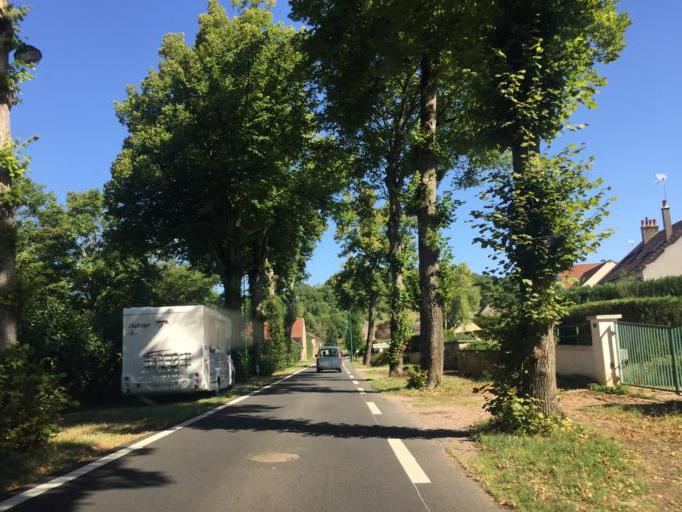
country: FR
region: Bourgogne
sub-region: Departement de la Nievre
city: Clamecy
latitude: 47.4552
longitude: 3.5506
